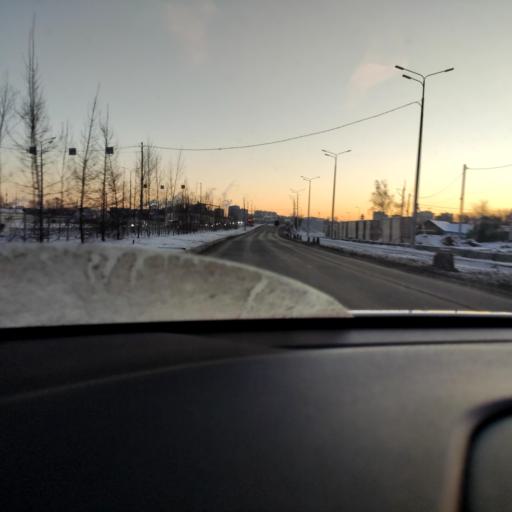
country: RU
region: Tatarstan
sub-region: Gorod Kazan'
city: Kazan
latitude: 55.7305
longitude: 49.1406
